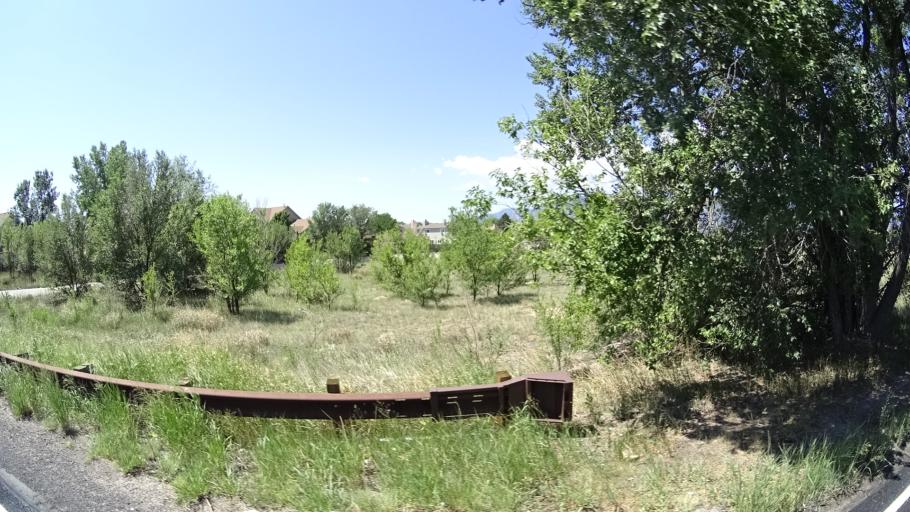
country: US
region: Colorado
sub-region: El Paso County
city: Stratmoor
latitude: 38.7874
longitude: -104.7409
